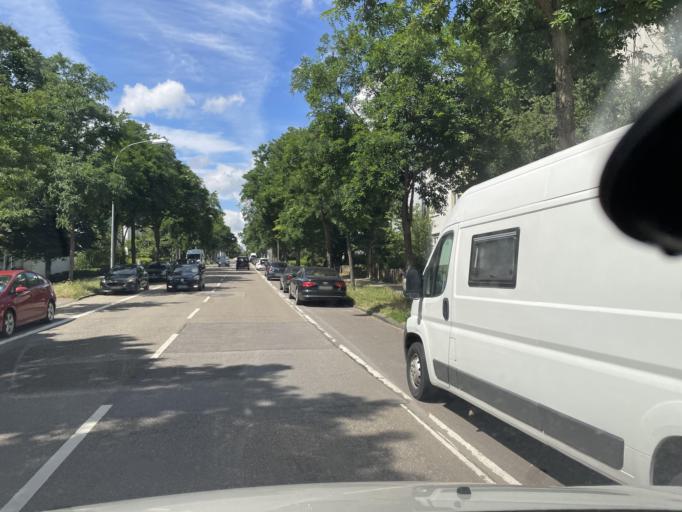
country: DE
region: Saarland
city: Saarbrucken
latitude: 49.2368
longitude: 7.0200
